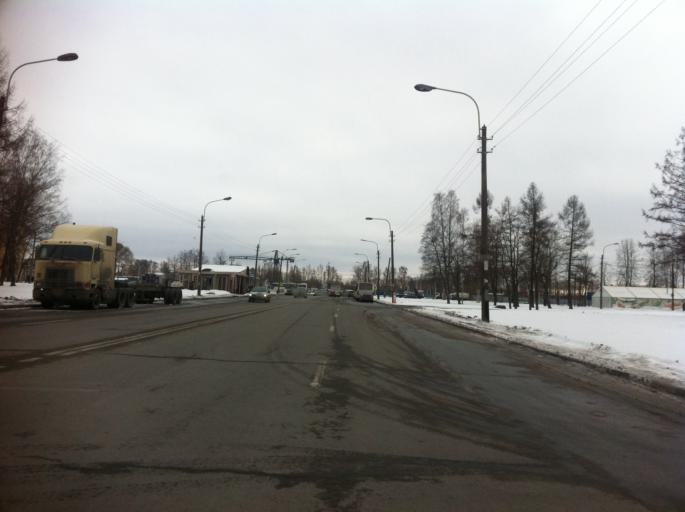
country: RU
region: St.-Petersburg
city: Uritsk
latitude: 59.8259
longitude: 30.1758
